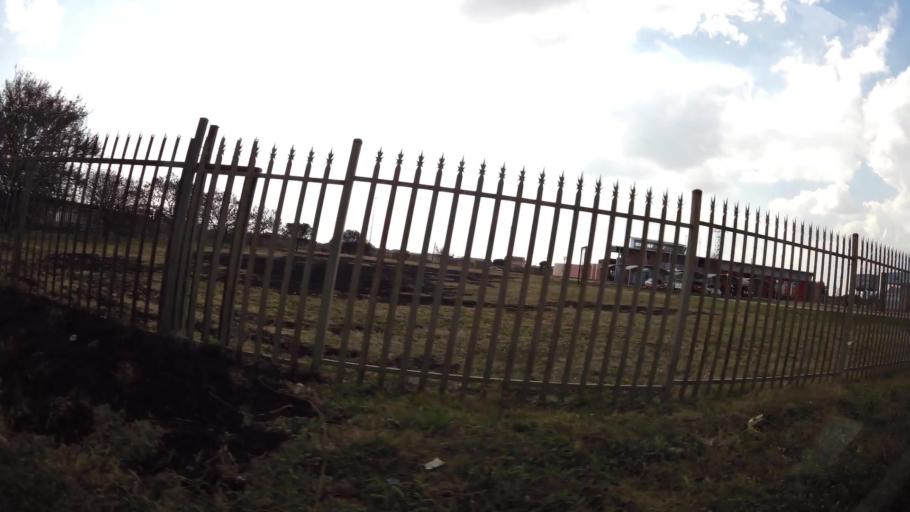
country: ZA
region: Gauteng
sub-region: Ekurhuleni Metropolitan Municipality
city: Springs
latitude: -26.1192
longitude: 28.4731
